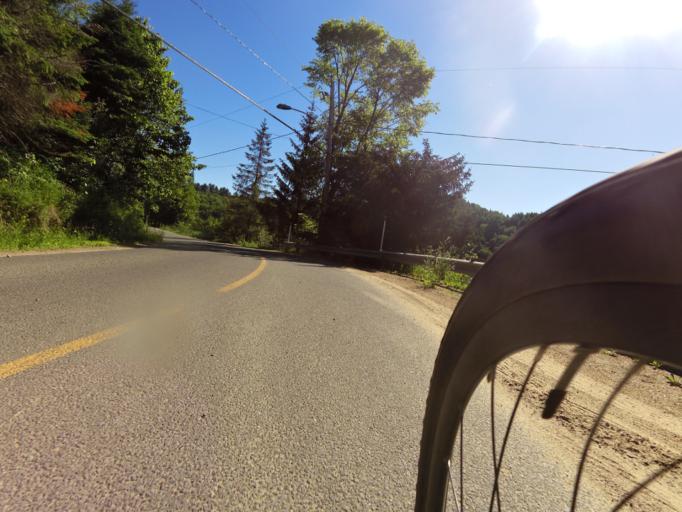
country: CA
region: Quebec
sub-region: Laurentides
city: Brownsburg-Chatham
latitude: 45.9038
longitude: -74.5969
